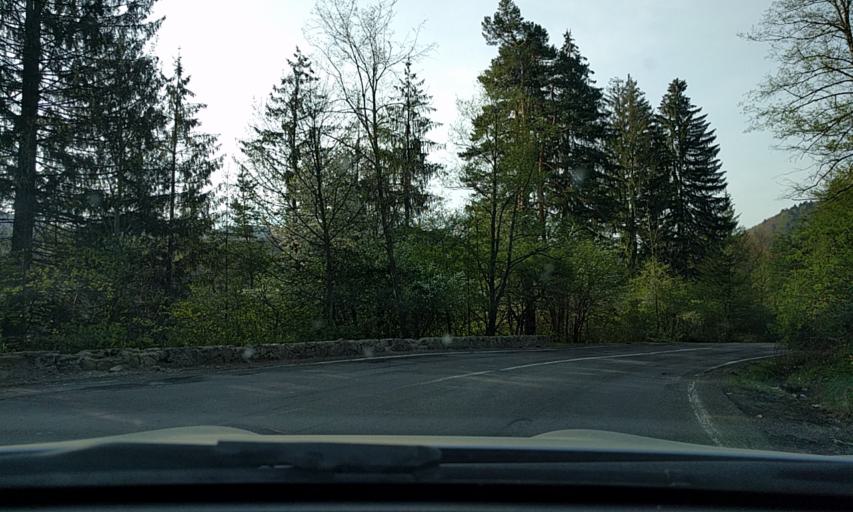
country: RO
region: Covasna
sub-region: Comuna Bretcu
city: Bretcu
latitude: 46.0693
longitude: 26.3836
